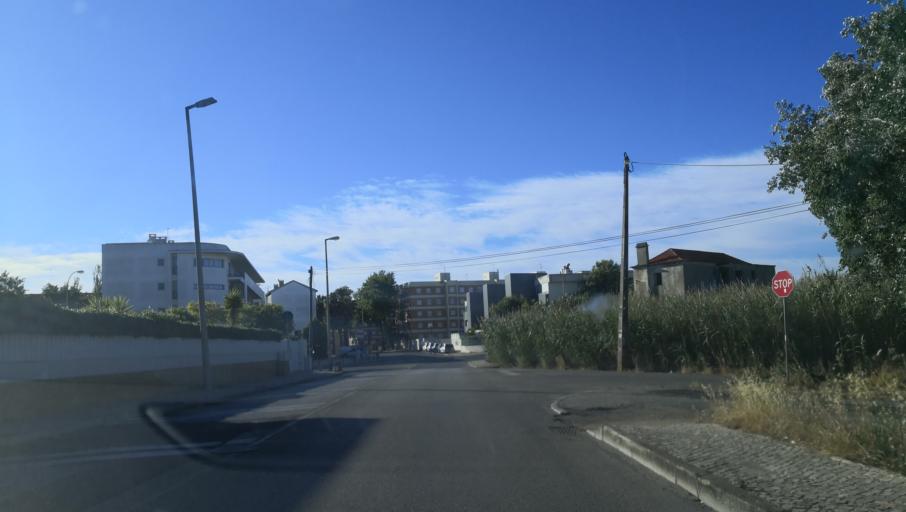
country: PT
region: Lisbon
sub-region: Oeiras
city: Carcavelos
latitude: 38.6838
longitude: -9.3250
